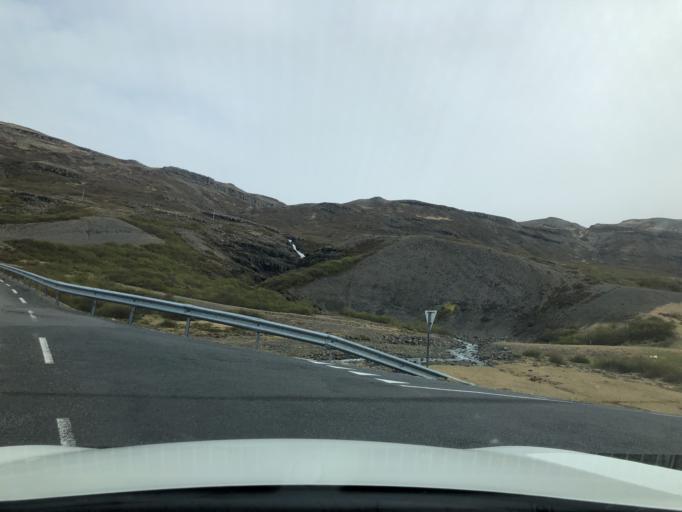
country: IS
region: Capital Region
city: Mosfellsbaer
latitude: 64.3853
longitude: -21.3548
